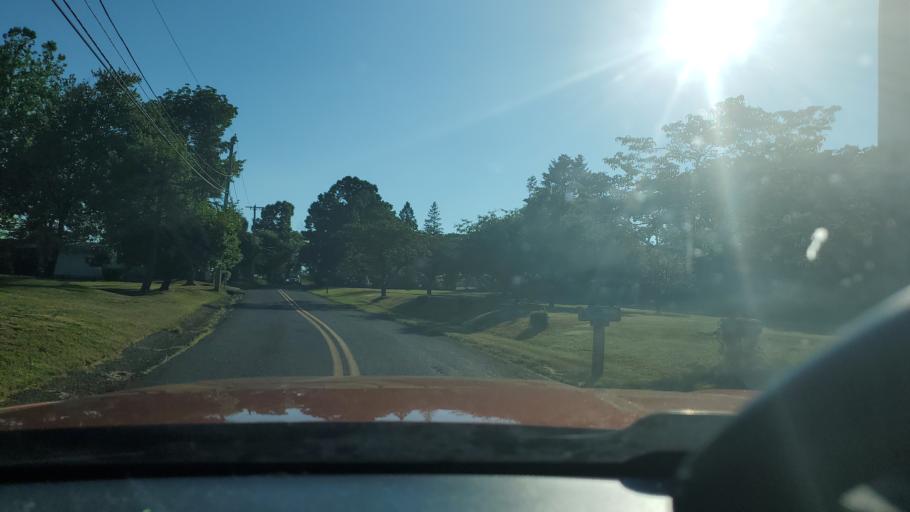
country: US
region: Pennsylvania
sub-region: Montgomery County
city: Woxall
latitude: 40.2982
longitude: -75.4453
